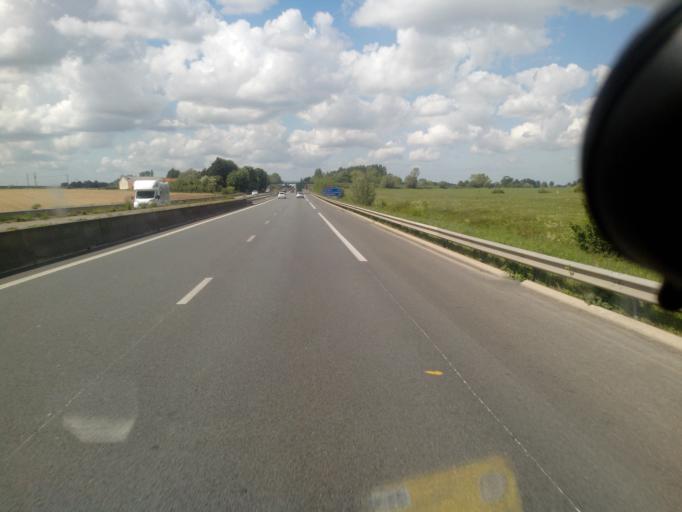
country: FR
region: Nord-Pas-de-Calais
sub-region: Departement du Nord
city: Steenvoorde
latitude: 50.8174
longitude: 2.5921
